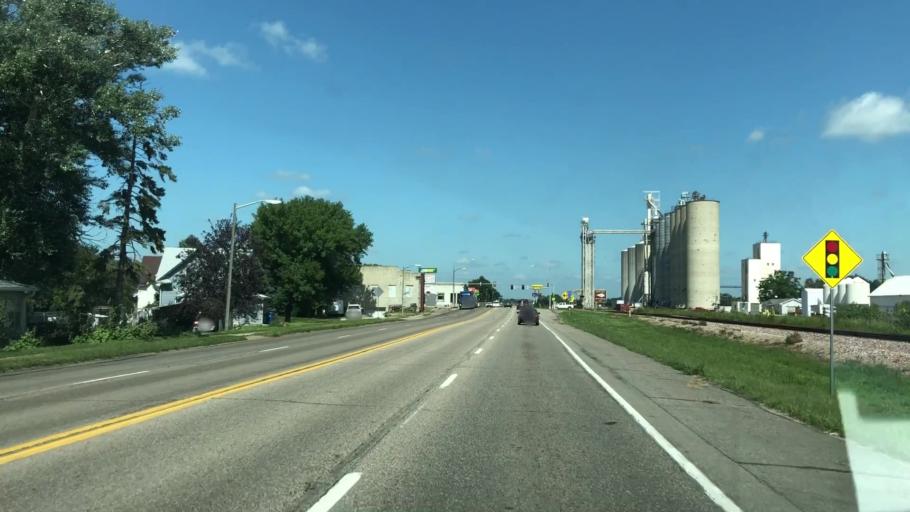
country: US
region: Iowa
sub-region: Woodbury County
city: Sioux City
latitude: 42.6247
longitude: -96.2924
